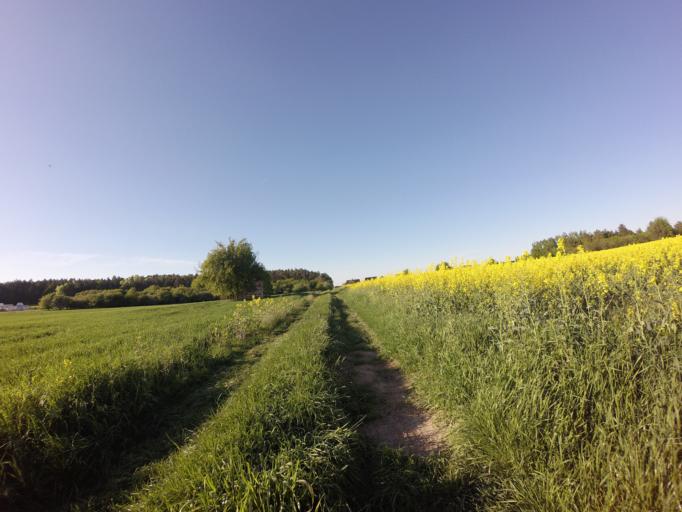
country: PL
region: West Pomeranian Voivodeship
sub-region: Powiat choszczenski
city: Choszczno
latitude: 53.1561
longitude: 15.3829
